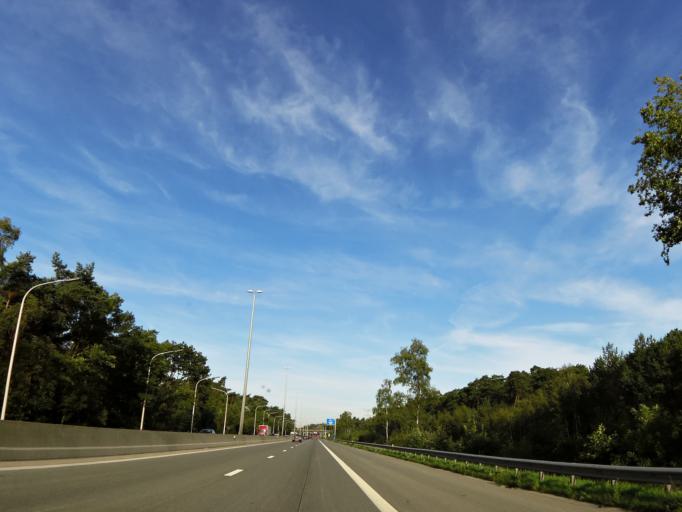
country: BE
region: Flanders
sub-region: Provincie Antwerpen
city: Vorselaar
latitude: 51.1731
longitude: 4.7643
